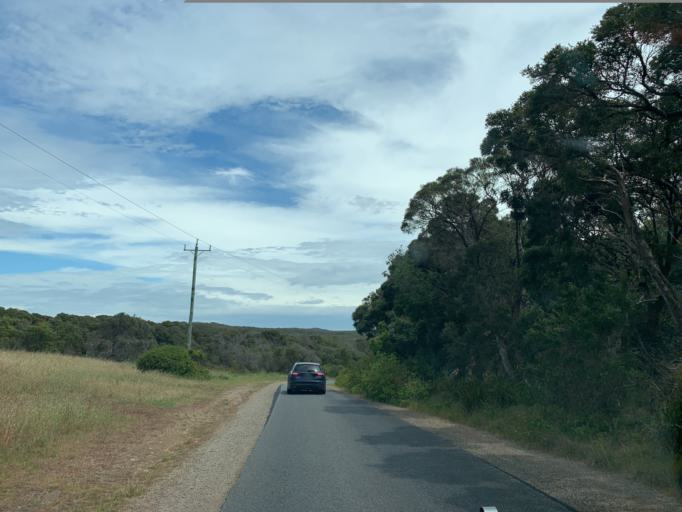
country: AU
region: Victoria
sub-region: Queenscliffe
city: Queenscliff
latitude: -38.3157
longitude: 144.6892
